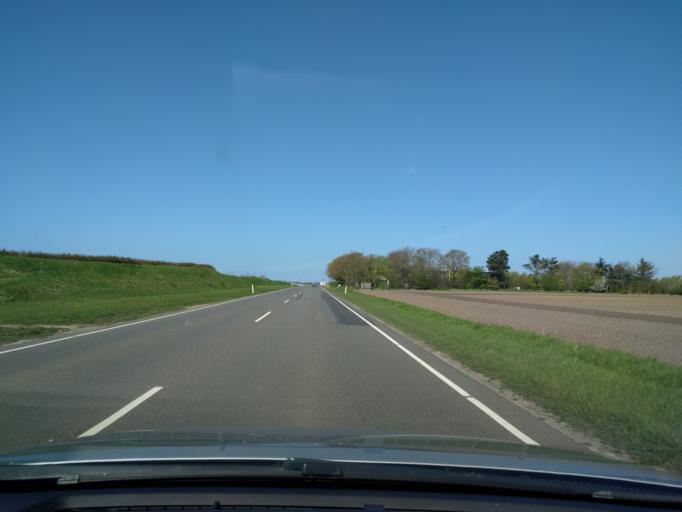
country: DK
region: Central Jutland
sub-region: Ringkobing-Skjern Kommune
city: Ringkobing
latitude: 56.1036
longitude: 8.2664
